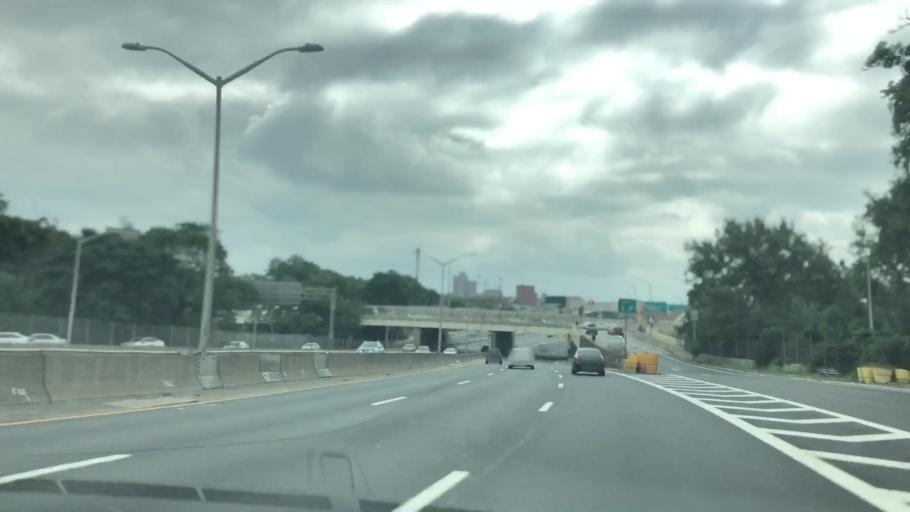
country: US
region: New York
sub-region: New York County
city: Inwood
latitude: 40.8297
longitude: -73.9321
